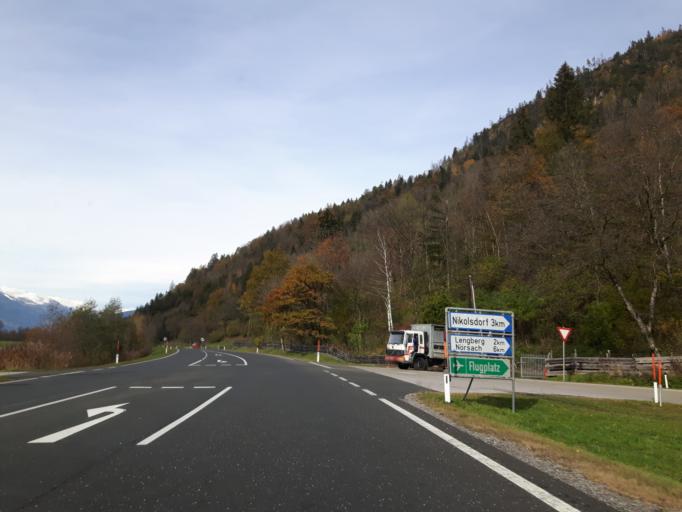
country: AT
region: Tyrol
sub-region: Politischer Bezirk Lienz
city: Lavant
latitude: 46.8021
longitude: 12.8717
